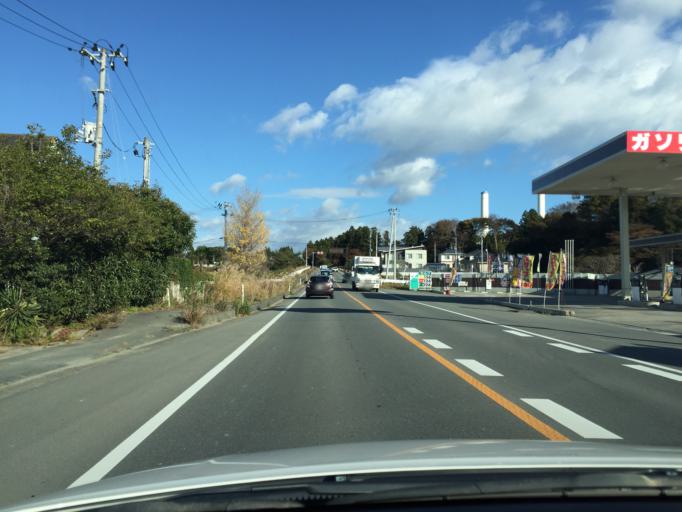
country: JP
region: Fukushima
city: Iwaki
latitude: 37.2209
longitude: 141.0020
